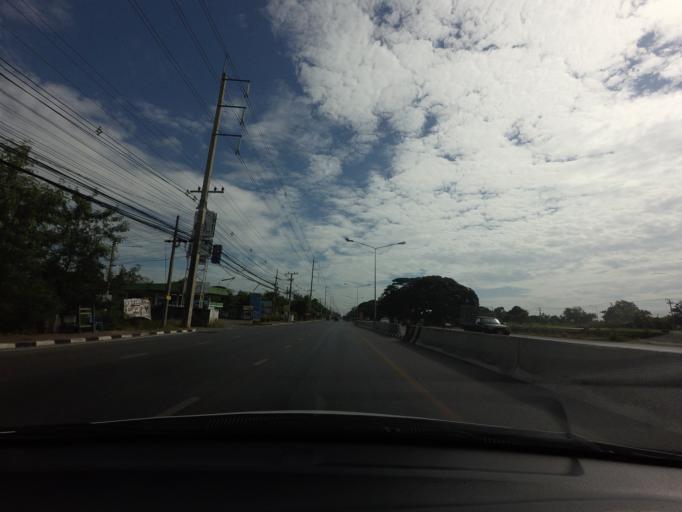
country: TH
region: Pathum Thani
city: Ban Rangsit
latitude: 14.0482
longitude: 100.8107
